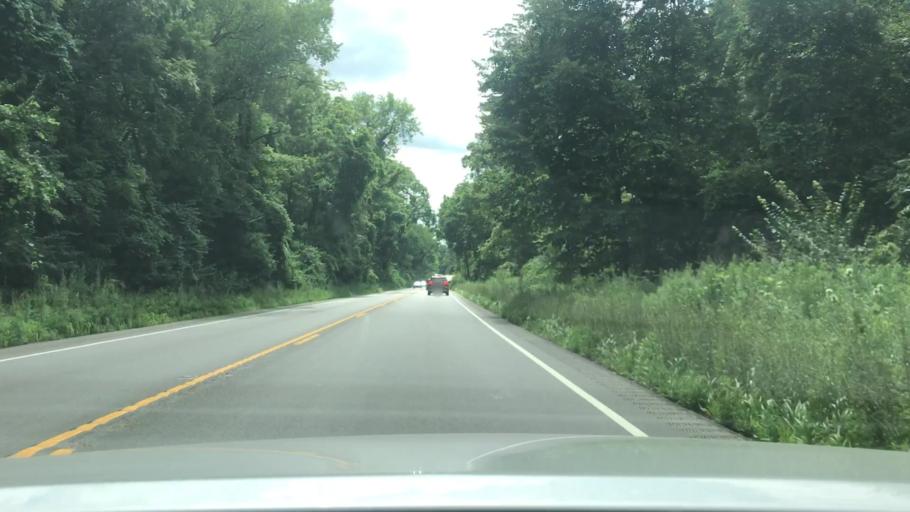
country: US
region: Illinois
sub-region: DuPage County
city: Burr Ridge
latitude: 41.7032
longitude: -87.9266
